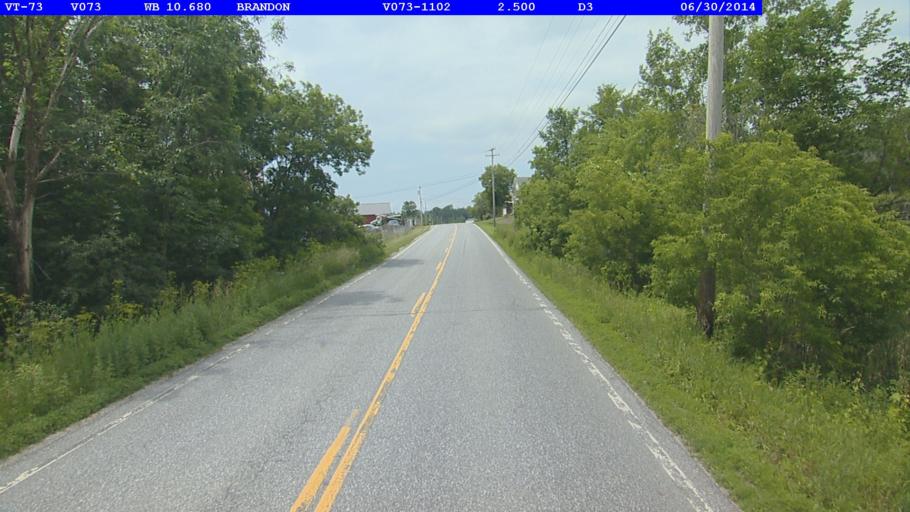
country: US
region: Vermont
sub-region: Rutland County
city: Brandon
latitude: 43.8009
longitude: -73.1039
